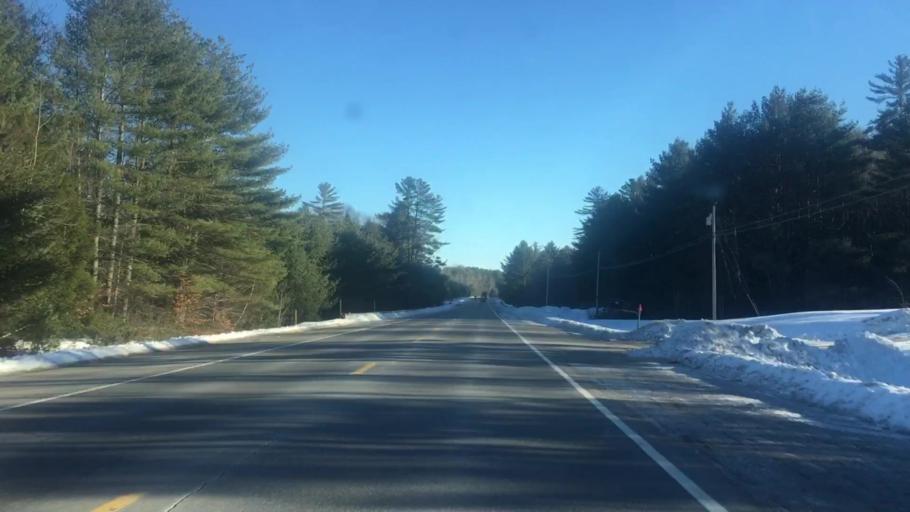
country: US
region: Maine
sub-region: Somerset County
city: Norridgewock
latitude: 44.6894
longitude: -69.7387
